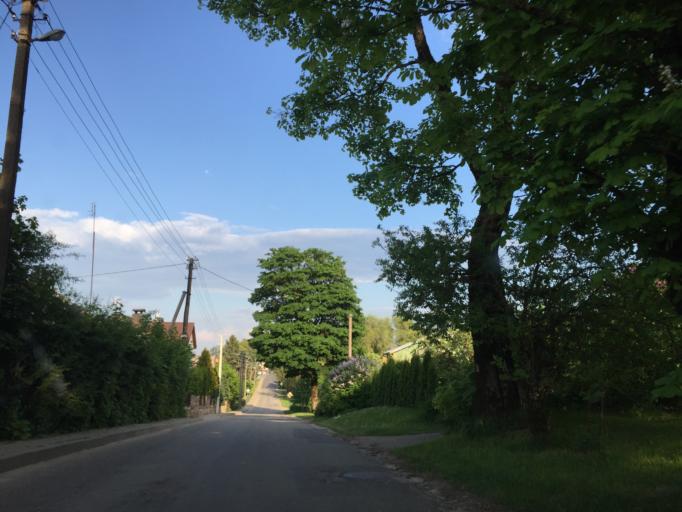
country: LT
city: Plateliai
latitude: 56.0441
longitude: 21.8110
